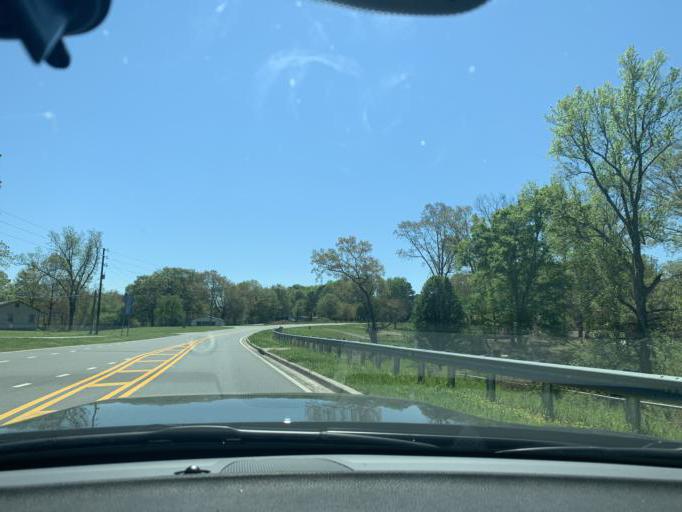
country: US
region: Georgia
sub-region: Forsyth County
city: Cumming
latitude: 34.1869
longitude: -84.1737
